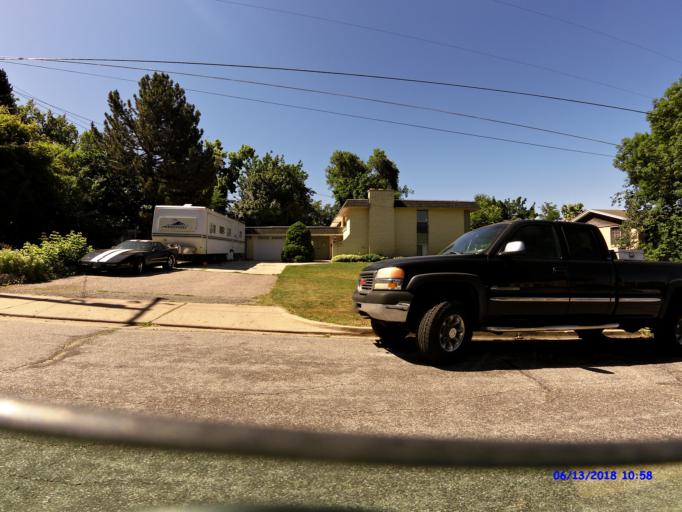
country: US
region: Utah
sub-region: Weber County
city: South Ogden
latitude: 41.2036
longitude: -111.9396
